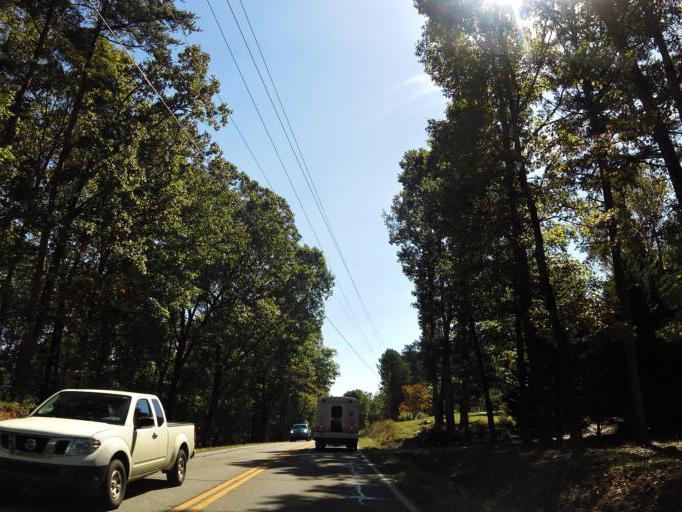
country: US
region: Georgia
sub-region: Pickens County
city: Nelson
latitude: 34.4142
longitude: -84.2962
